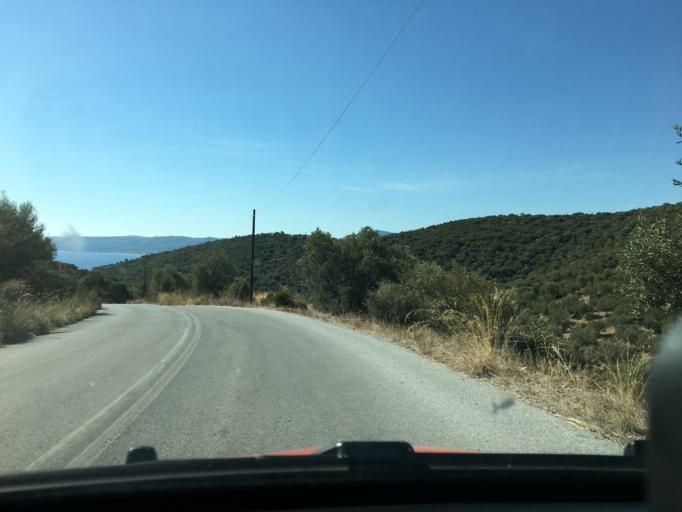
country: GR
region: Central Macedonia
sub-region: Nomos Chalkidikis
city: Agios Nikolaos
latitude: 40.3415
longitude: 23.7217
